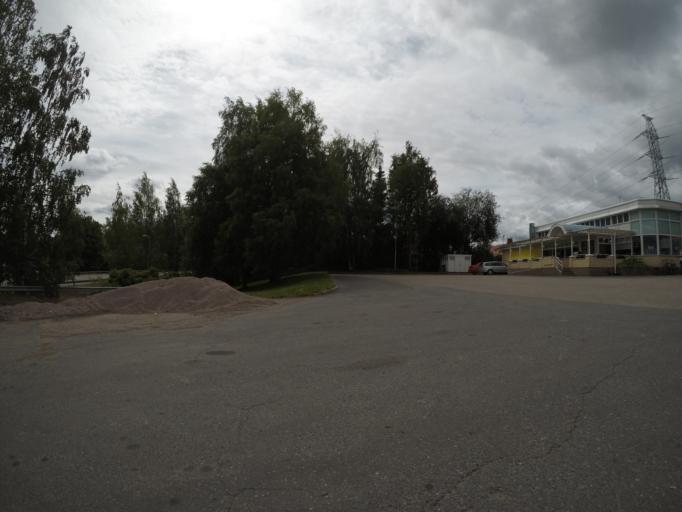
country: FI
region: Haeme
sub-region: Haemeenlinna
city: Haemeenlinna
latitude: 61.0051
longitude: 24.5064
